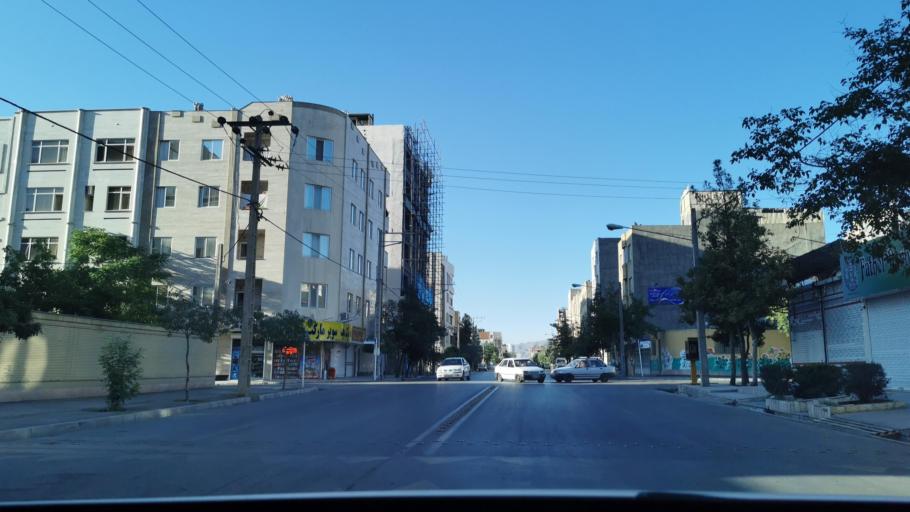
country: IR
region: Razavi Khorasan
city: Mashhad
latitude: 36.3571
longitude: 59.4972
